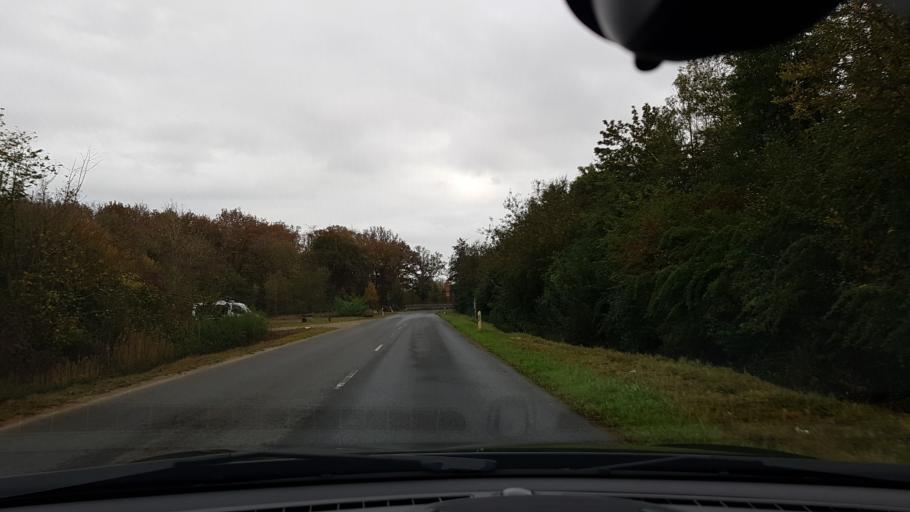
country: DE
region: North Rhine-Westphalia
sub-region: Regierungsbezirk Koln
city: Elsdorf
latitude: 50.9313
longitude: 6.5497
